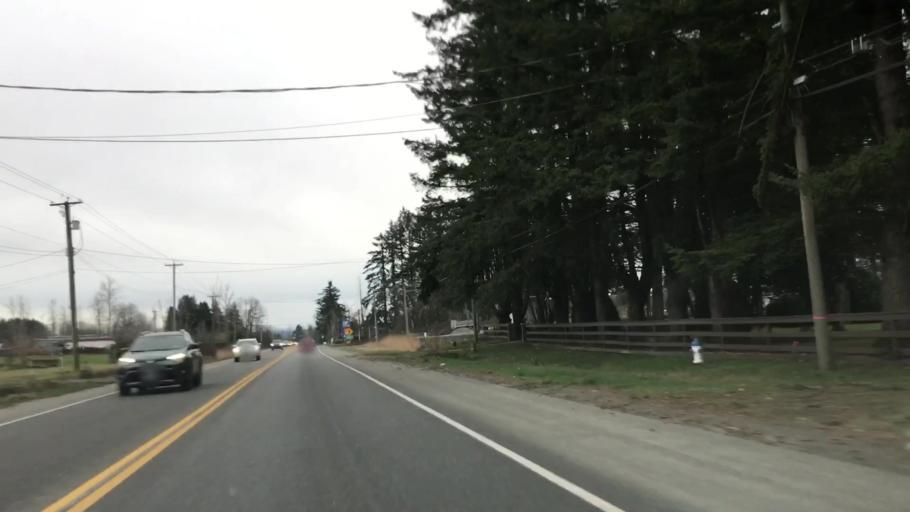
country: CA
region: British Columbia
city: Aldergrove
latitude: 49.0572
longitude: -122.4439
